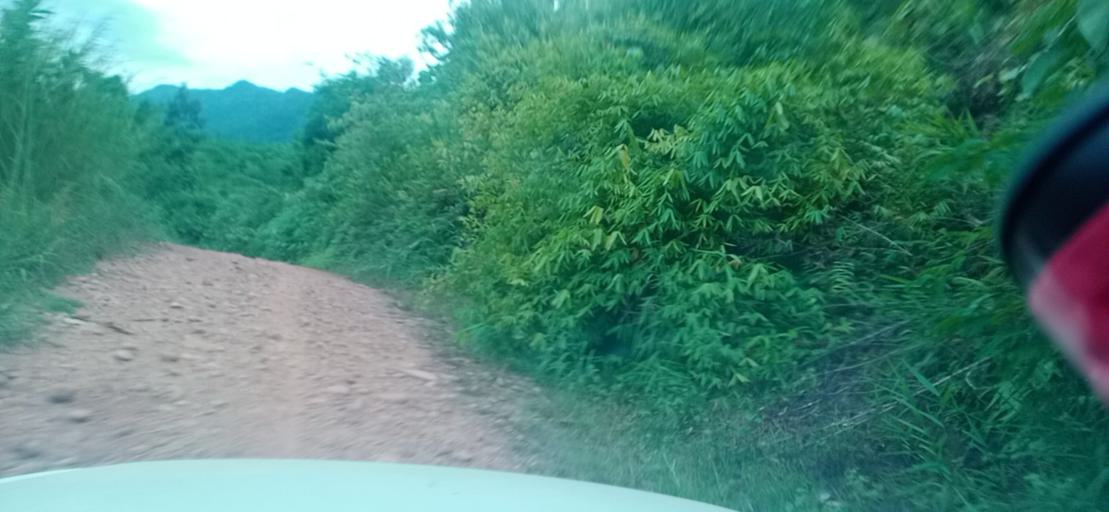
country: TH
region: Changwat Bueng Kan
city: Pak Khat
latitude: 18.5600
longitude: 103.2932
